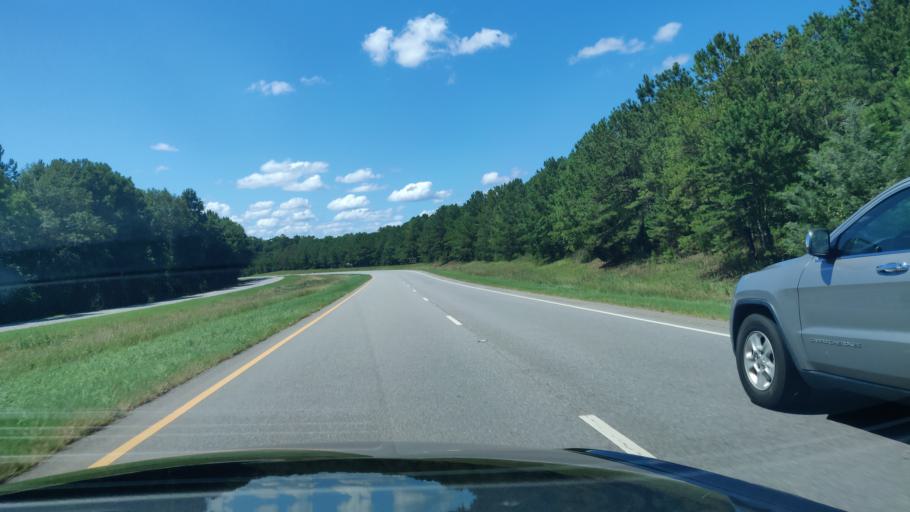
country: US
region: Georgia
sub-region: Terrell County
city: Dawson
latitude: 31.8644
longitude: -84.4839
